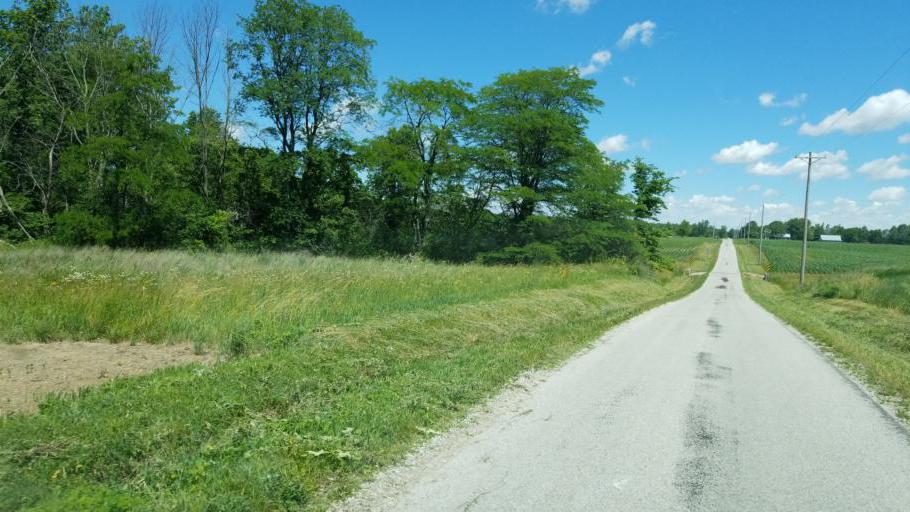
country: US
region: Ohio
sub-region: Crawford County
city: Bucyrus
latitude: 40.6818
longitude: -82.9390
